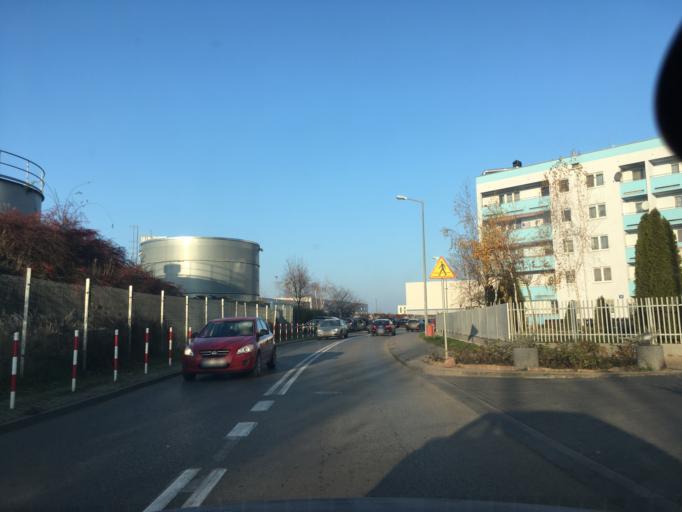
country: PL
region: Masovian Voivodeship
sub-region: Powiat piaseczynski
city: Piaseczno
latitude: 52.0778
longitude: 21.0093
